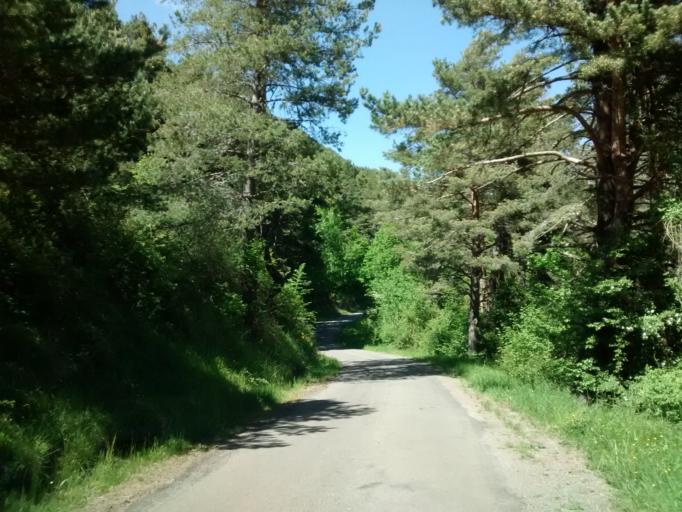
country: ES
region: Aragon
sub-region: Provincia de Huesca
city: Borau
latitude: 42.7127
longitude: -0.6083
